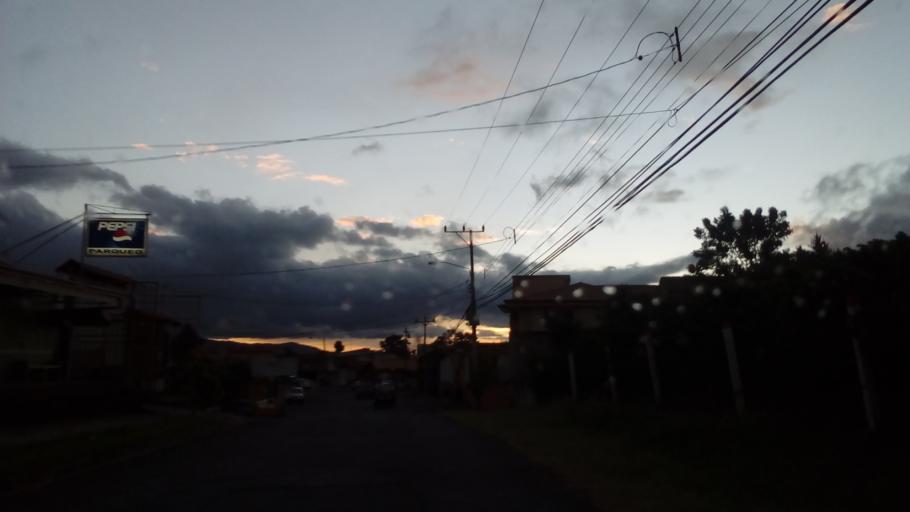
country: CR
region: Heredia
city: San Pablo
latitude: 9.9999
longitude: -84.0905
